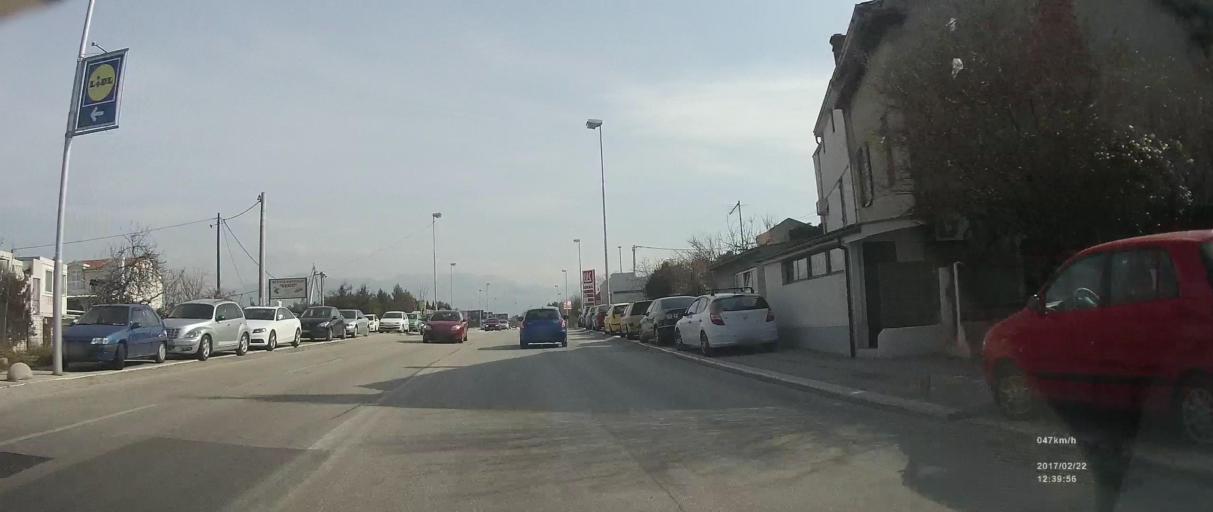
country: HR
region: Splitsko-Dalmatinska
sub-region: Grad Split
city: Split
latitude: 43.5219
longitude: 16.4348
